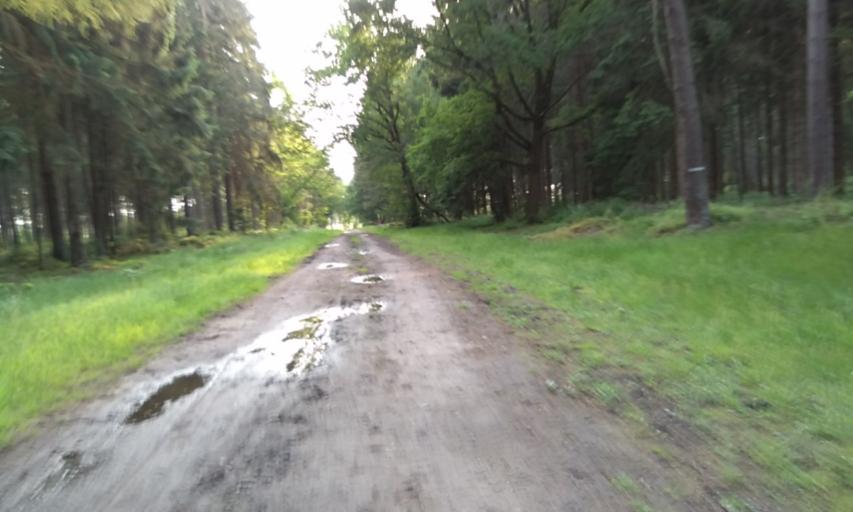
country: DE
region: Lower Saxony
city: Agathenburg
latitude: 53.5313
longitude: 9.5020
